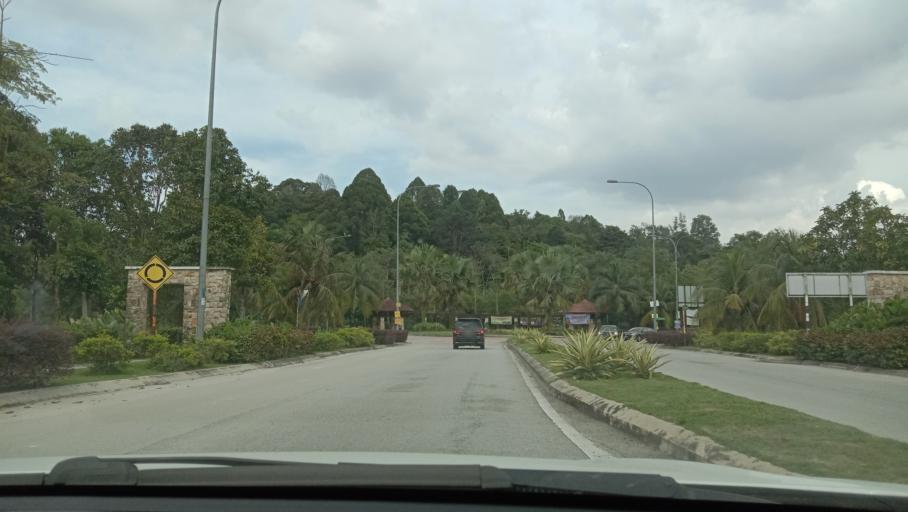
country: MY
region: Selangor
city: Kampung Baru Subang
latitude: 3.1350
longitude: 101.5015
